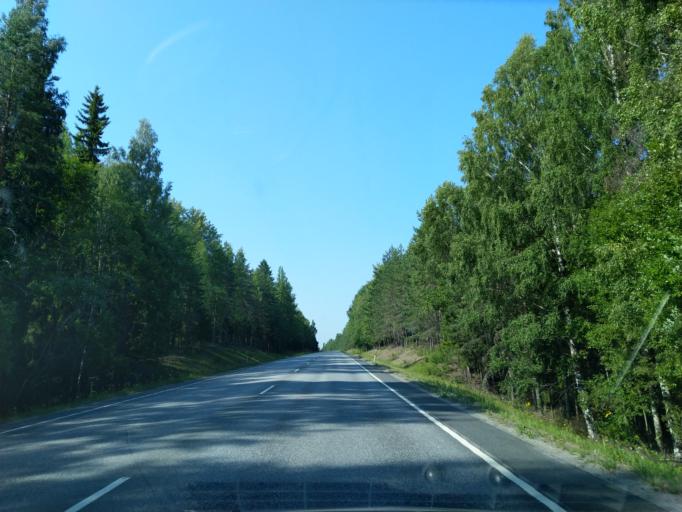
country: FI
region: Satakunta
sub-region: Pori
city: Noormarkku
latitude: 61.6205
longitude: 21.9072
